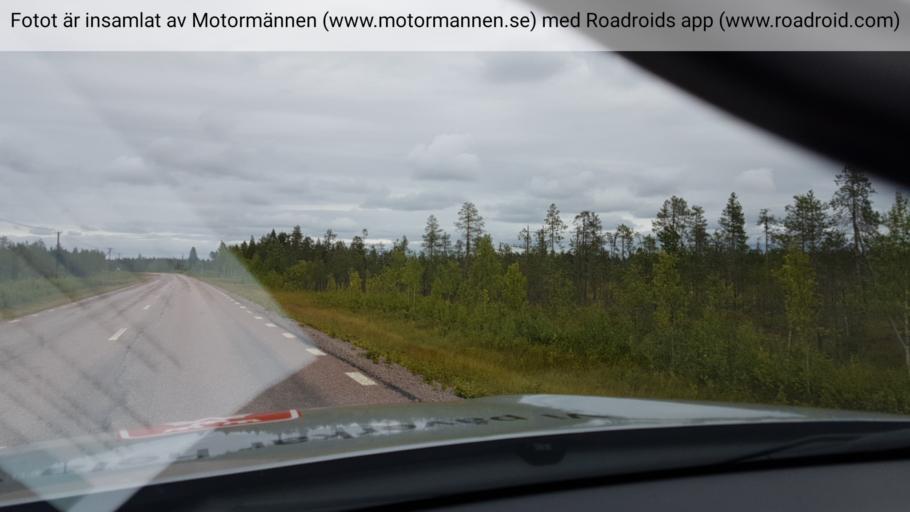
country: SE
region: Norrbotten
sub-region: Pajala Kommun
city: Pajala
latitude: 67.1009
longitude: 22.5876
